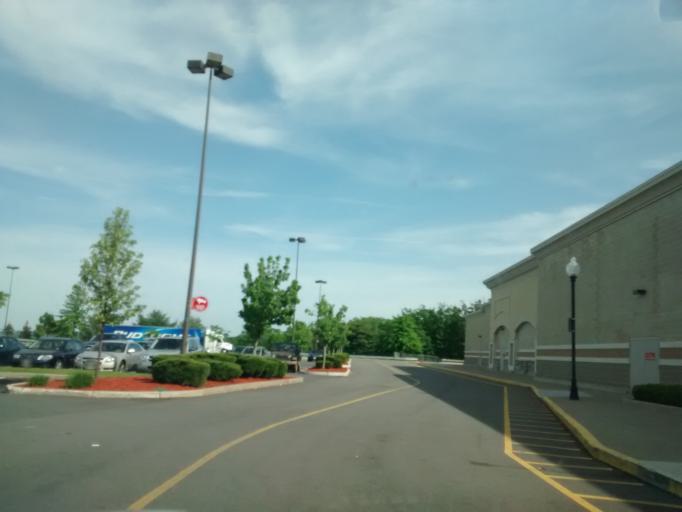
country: US
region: Massachusetts
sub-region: Worcester County
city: Millbury
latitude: 42.1942
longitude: -71.7745
